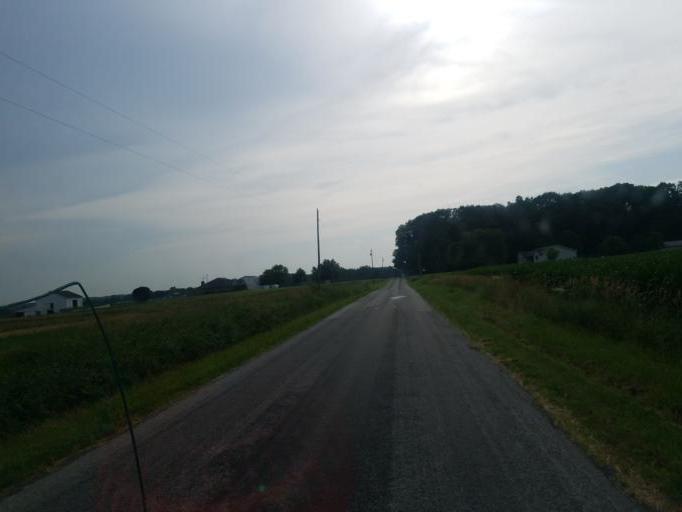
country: US
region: Ohio
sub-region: Wayne County
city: West Salem
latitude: 40.9009
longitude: -82.1247
